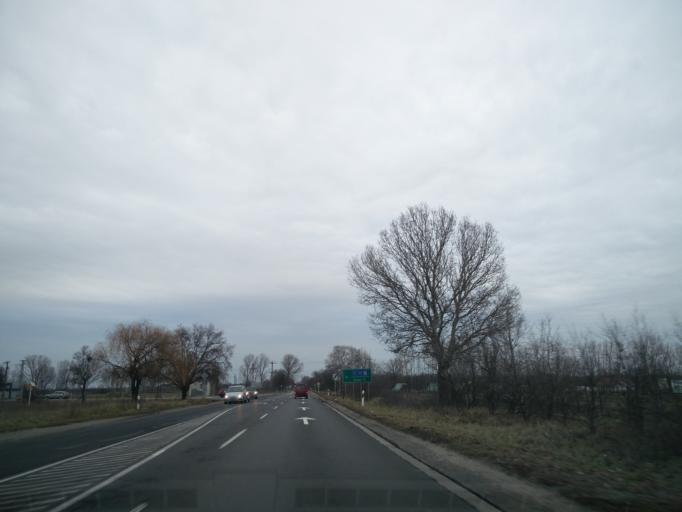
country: HU
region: Pest
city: Vecses
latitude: 47.4010
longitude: 19.2953
